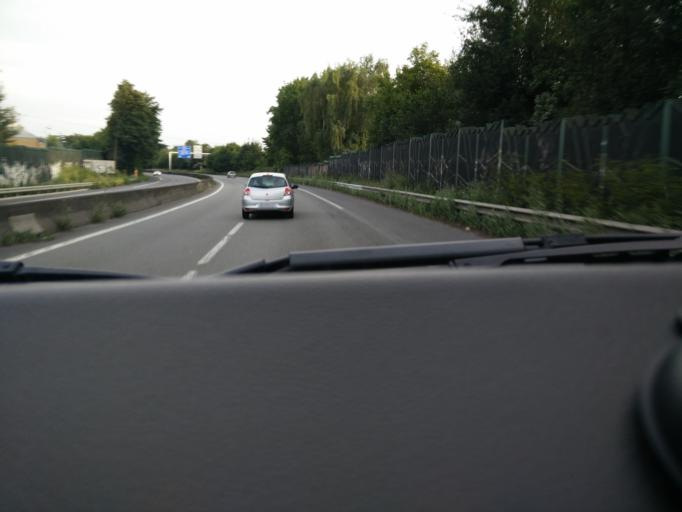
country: FR
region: Nord-Pas-de-Calais
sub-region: Departement du Nord
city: La Sentinelle
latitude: 50.3508
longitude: 3.4789
